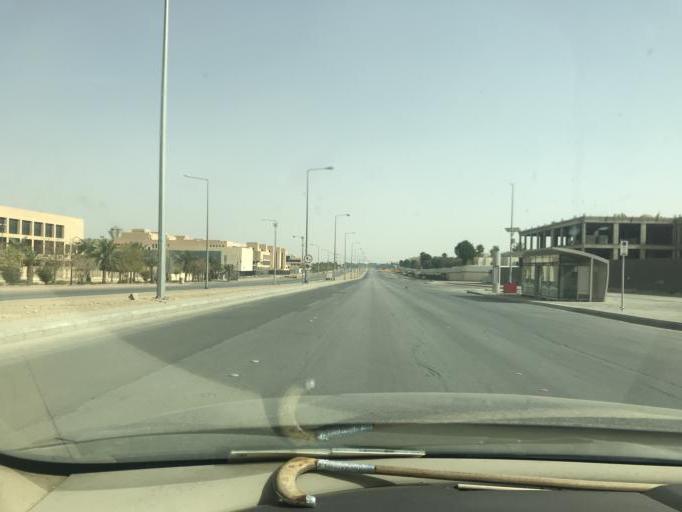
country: SA
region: Ar Riyad
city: Riyadh
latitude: 24.8139
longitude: 46.6896
